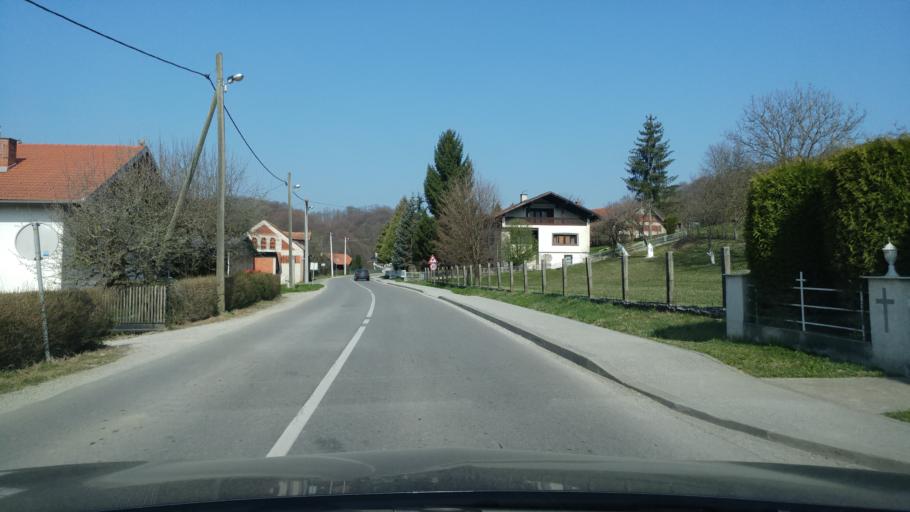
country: HR
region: Zagrebacka
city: Pojatno
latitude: 45.9456
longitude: 15.7500
